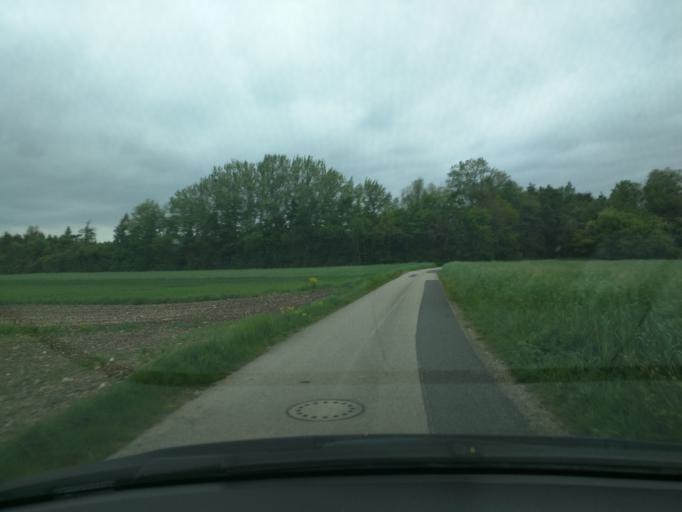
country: AT
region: Lower Austria
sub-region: Politischer Bezirk Amstetten
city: Sankt Georgen am Ybbsfelde
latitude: 48.1128
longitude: 14.9558
